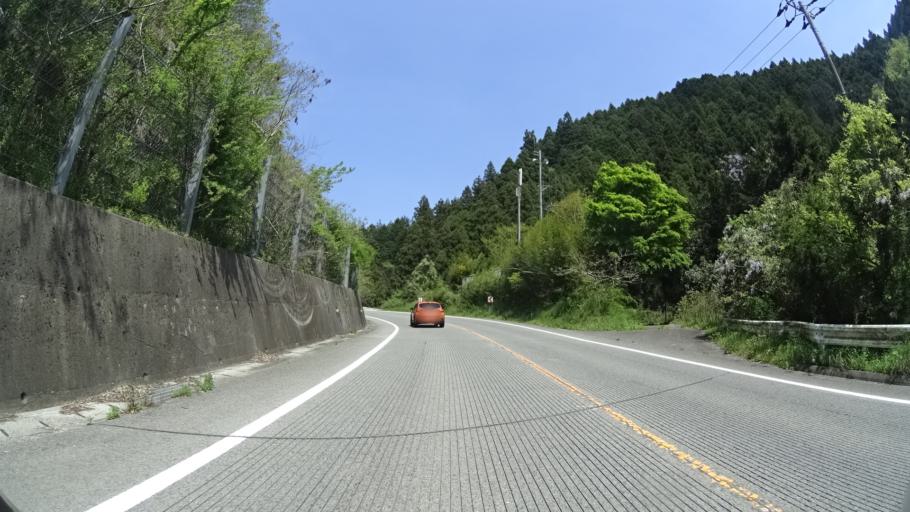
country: JP
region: Ehime
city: Hojo
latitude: 33.9239
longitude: 132.8889
